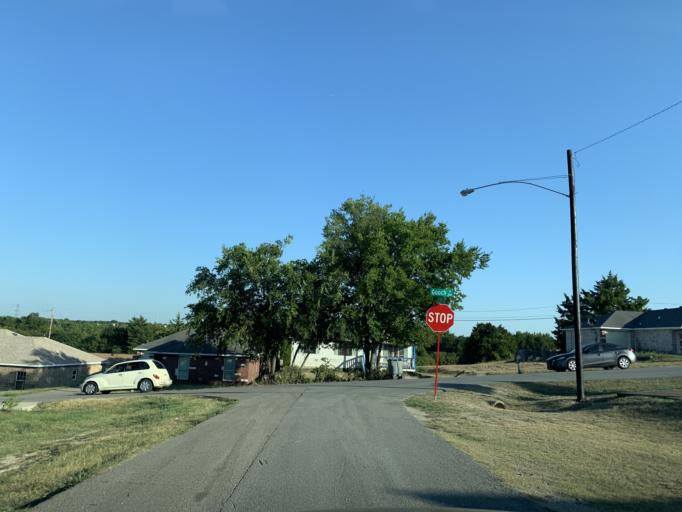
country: US
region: Texas
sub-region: Dallas County
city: Hutchins
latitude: 32.6738
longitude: -96.7771
